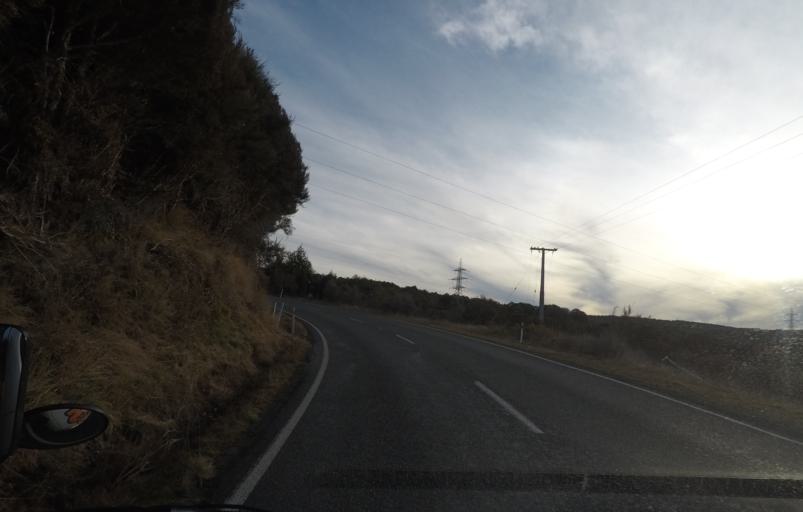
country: NZ
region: Tasman
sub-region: Tasman District
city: Wakefield
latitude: -41.7637
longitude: 172.8938
